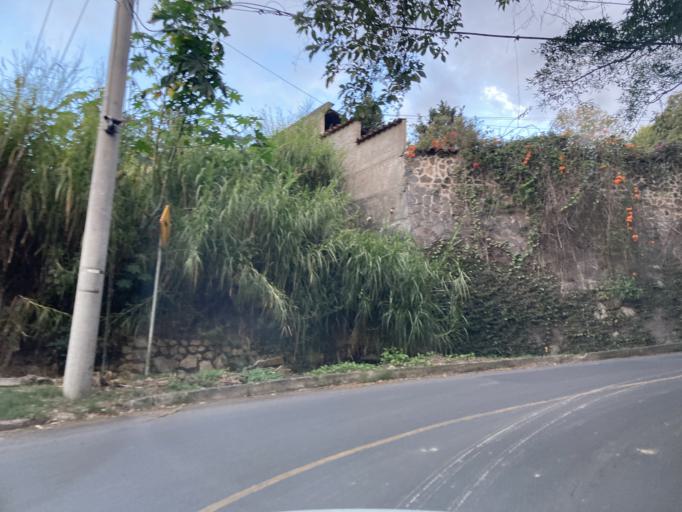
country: GT
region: Guatemala
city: Santa Catarina Pinula
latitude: 14.5567
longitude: -90.4615
